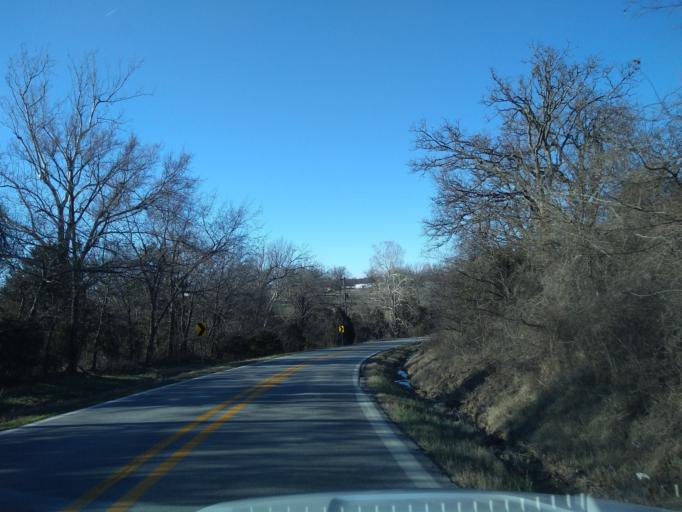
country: US
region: Arkansas
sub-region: Washington County
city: Lincoln
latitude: 35.9473
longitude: -94.3769
